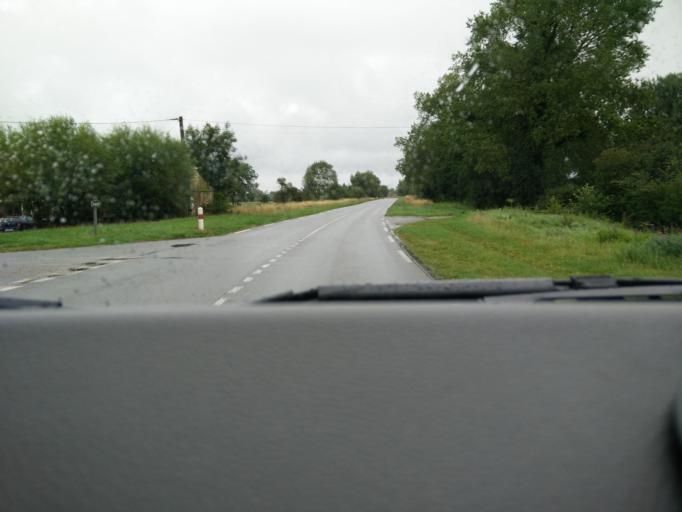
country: FR
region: Picardie
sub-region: Departement de la Somme
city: Rue
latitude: 50.2485
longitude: 1.6524
